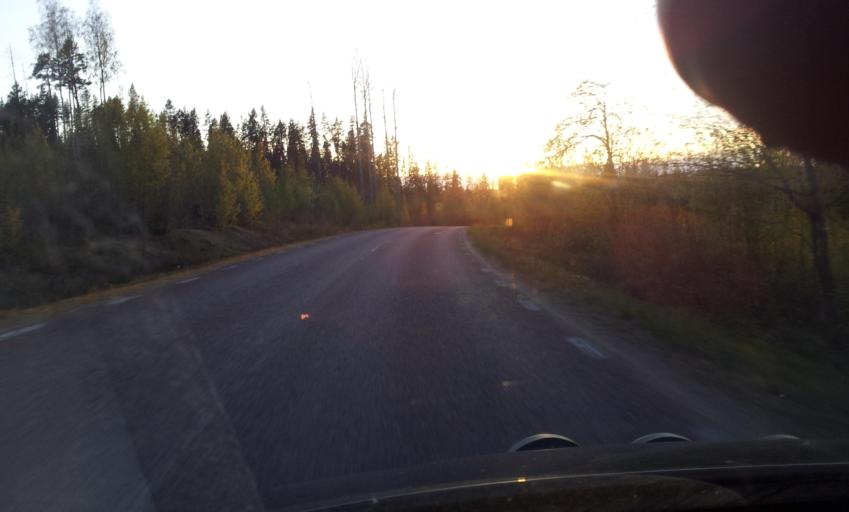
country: SE
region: Gaevleborg
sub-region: Bollnas Kommun
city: Bollnas
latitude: 61.3895
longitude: 16.4661
